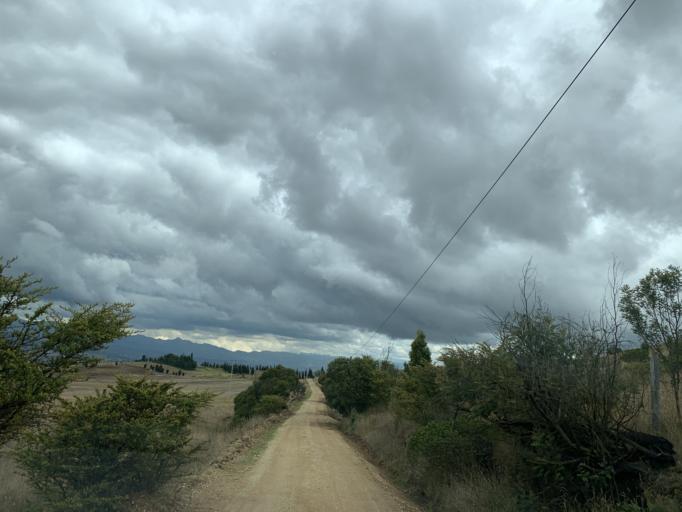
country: CO
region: Boyaca
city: Tunja
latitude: 5.5552
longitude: -73.3161
